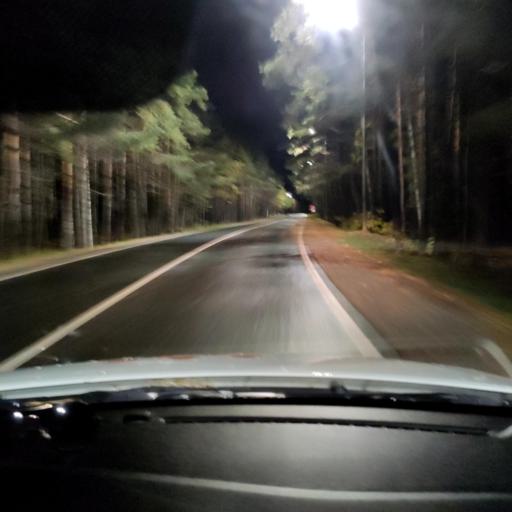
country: RU
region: Tatarstan
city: Verkhniy Uslon
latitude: 55.6345
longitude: 49.0192
